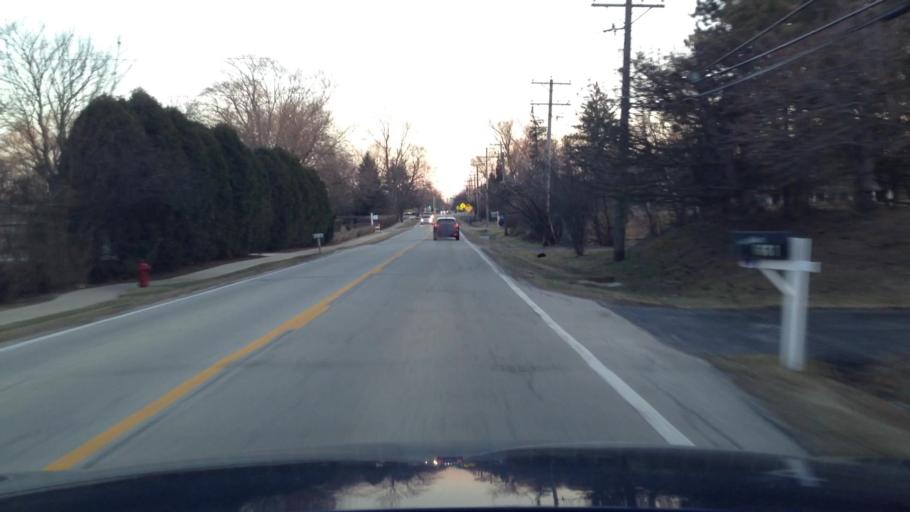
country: US
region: Illinois
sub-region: Cook County
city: Northfield
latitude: 42.1097
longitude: -87.7902
